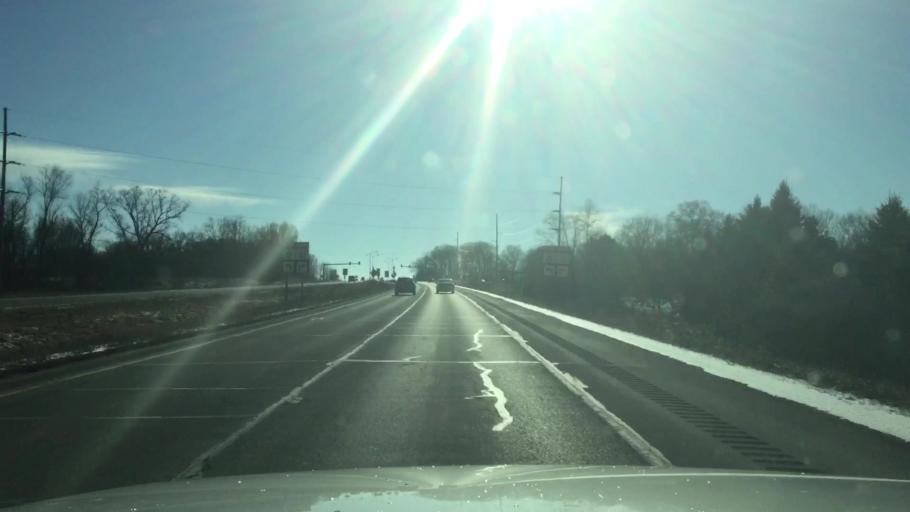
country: US
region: Wisconsin
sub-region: Racine County
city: Rochester
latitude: 42.7448
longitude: -88.2142
